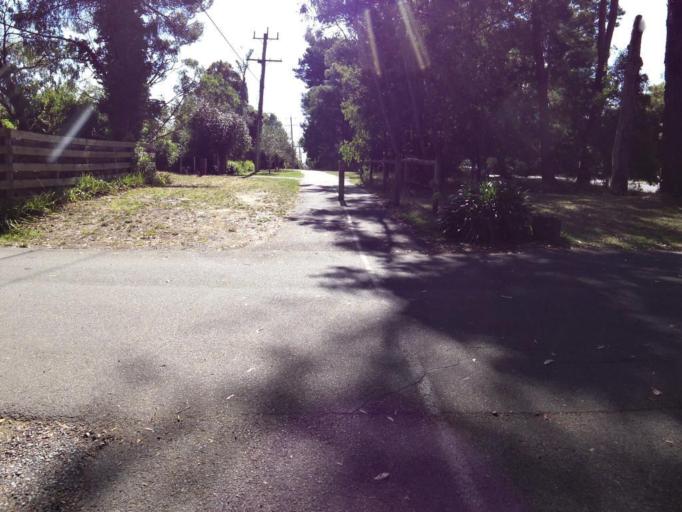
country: AU
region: Victoria
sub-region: Yarra Ranges
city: Kilsyth
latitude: -37.8008
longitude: 145.3318
